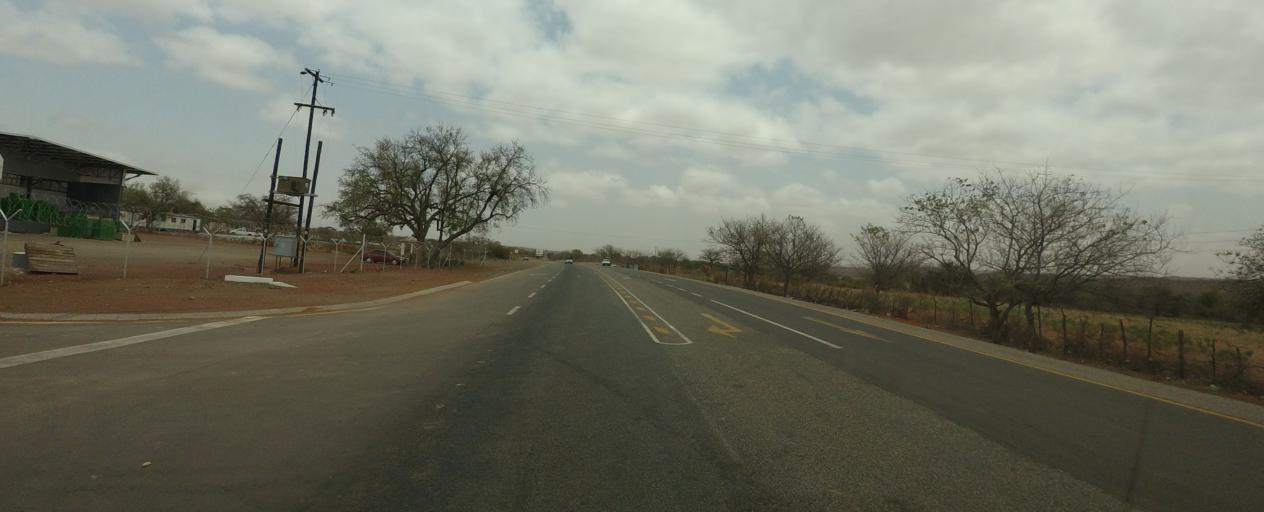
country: ZA
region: Limpopo
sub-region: Vhembe District Municipality
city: Mutale
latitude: -22.4519
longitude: 30.5028
